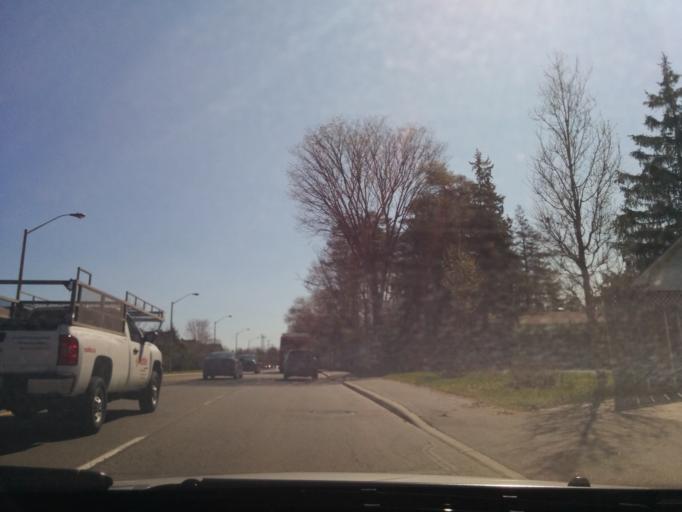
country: CA
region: Ontario
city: Ottawa
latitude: 45.3986
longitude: -75.6577
